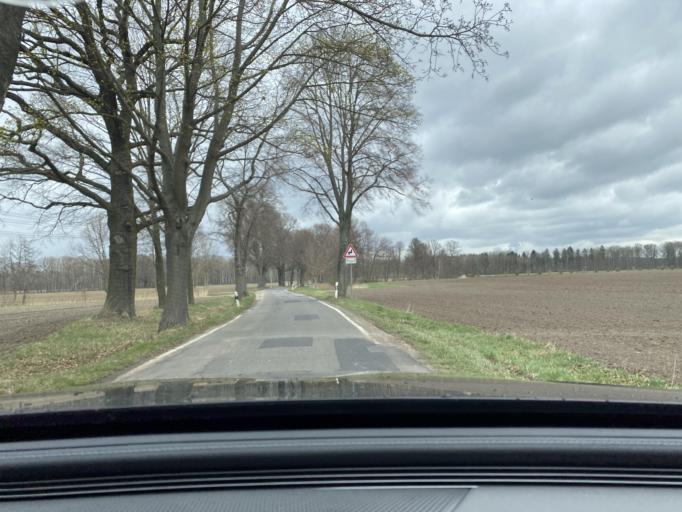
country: DE
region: Saxony
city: Uhyst
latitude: 51.3187
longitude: 14.4666
